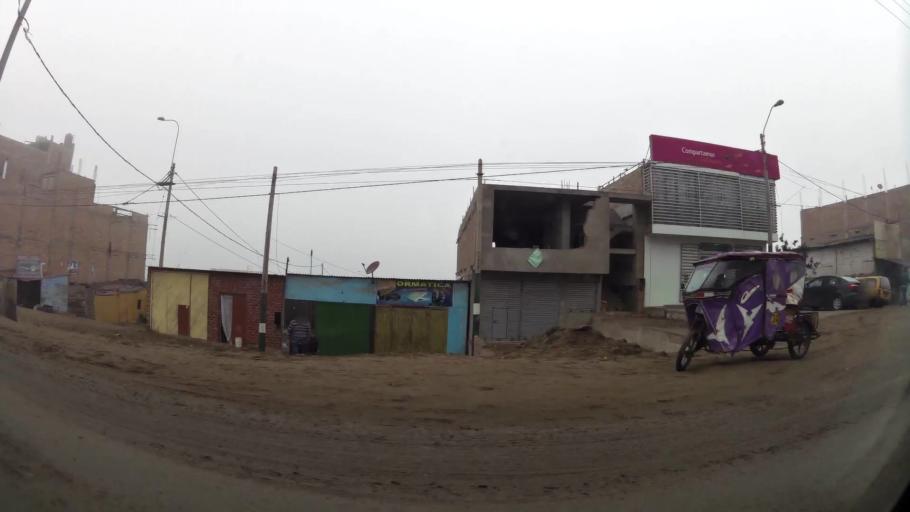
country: PE
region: Lima
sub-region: Lima
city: Santa Rosa
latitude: -11.8326
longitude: -77.1437
